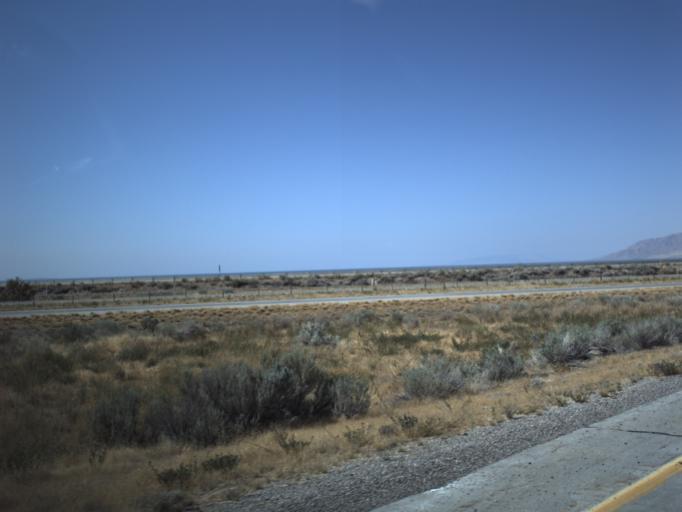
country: US
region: Utah
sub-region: Salt Lake County
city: Magna
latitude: 40.7474
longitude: -112.1793
